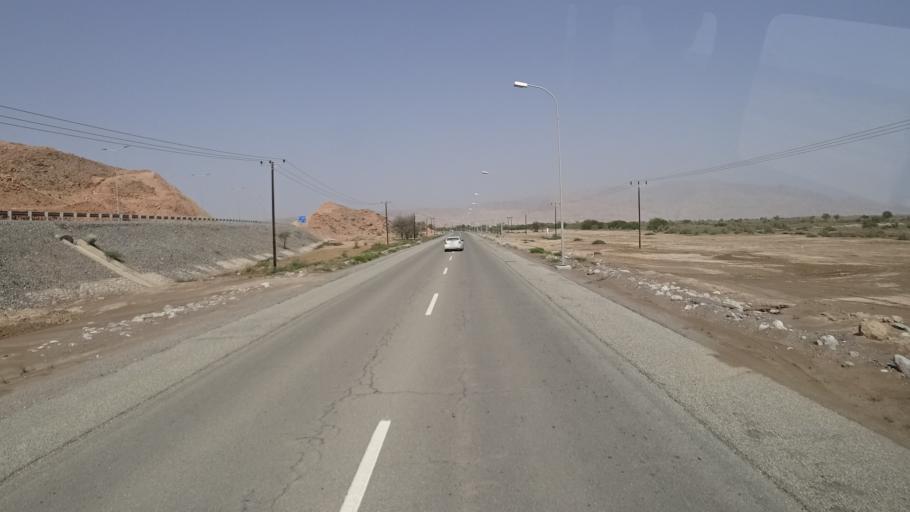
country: OM
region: Muhafazat Masqat
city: Muscat
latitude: 23.2131
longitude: 58.9373
